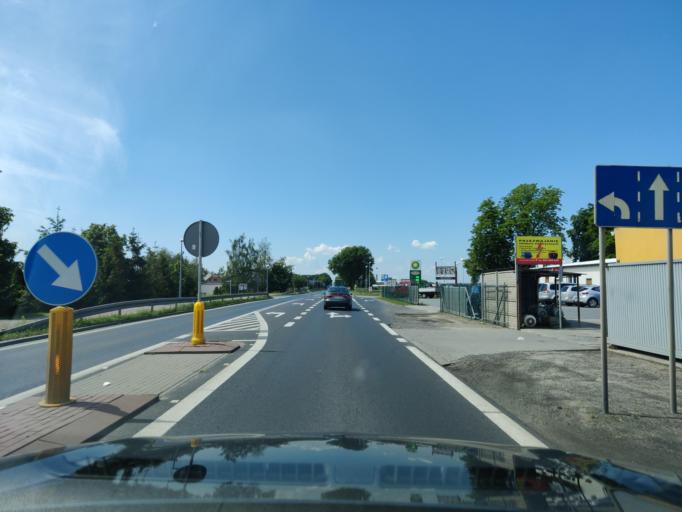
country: PL
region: Greater Poland Voivodeship
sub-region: Powiat grodziski
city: Rakoniewice
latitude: 52.1467
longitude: 16.2855
